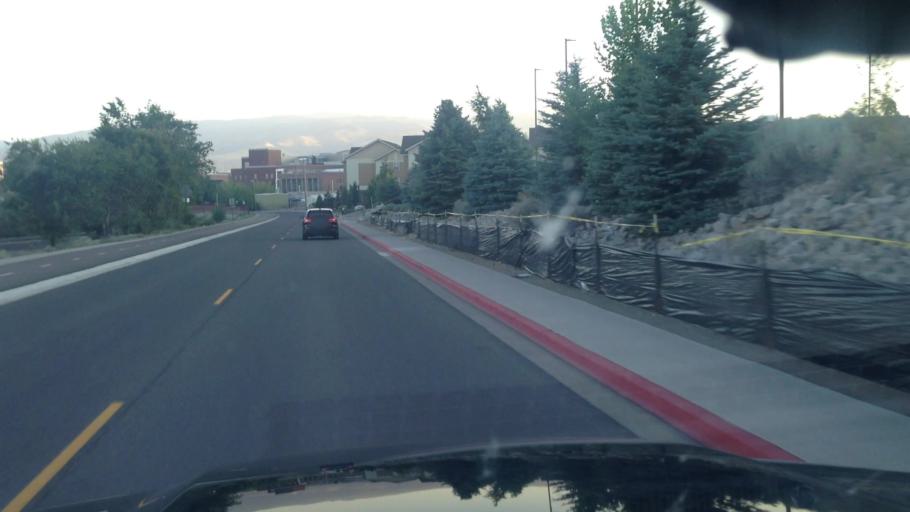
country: US
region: Nevada
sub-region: Washoe County
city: Reno
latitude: 39.5473
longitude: -119.8123
